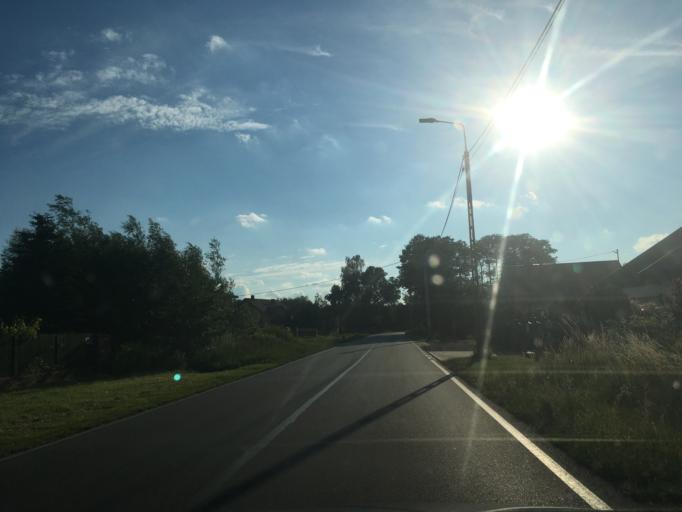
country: PL
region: Masovian Voivodeship
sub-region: Powiat wolominski
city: Radzymin
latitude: 52.4114
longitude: 21.2227
